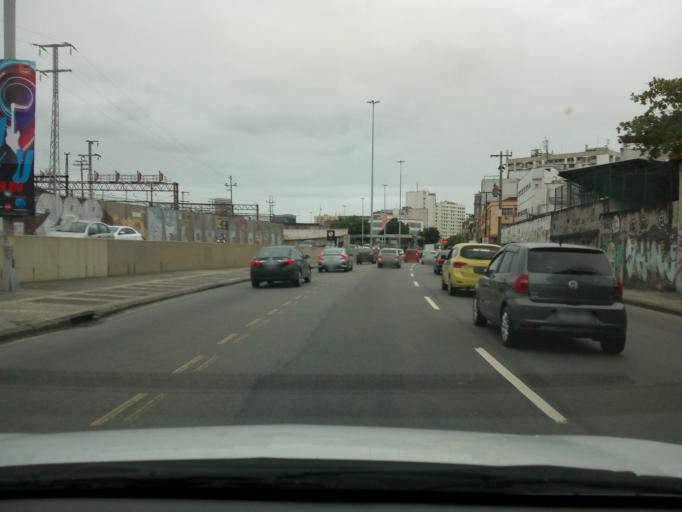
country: BR
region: Rio de Janeiro
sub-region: Rio De Janeiro
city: Rio de Janeiro
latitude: -22.9105
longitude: -43.2196
